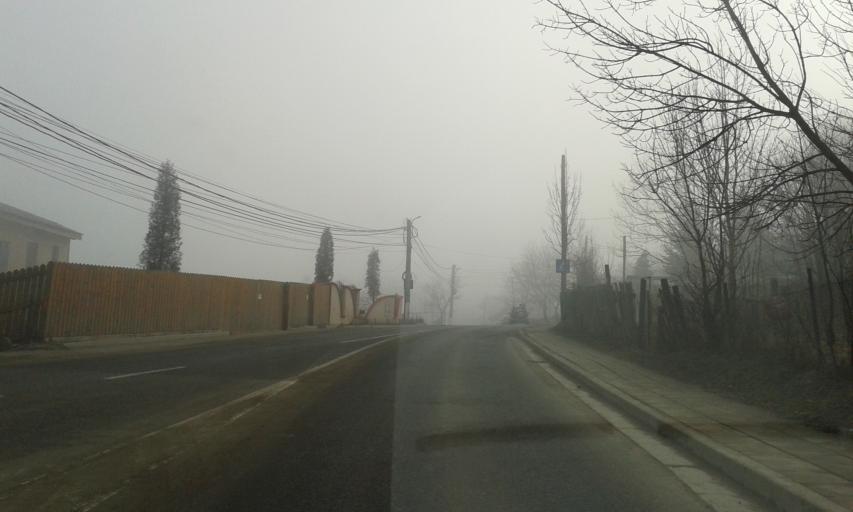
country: RO
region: Hunedoara
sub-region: Comuna Aninoasa
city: Aninoasa
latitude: 45.3752
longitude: 23.3049
